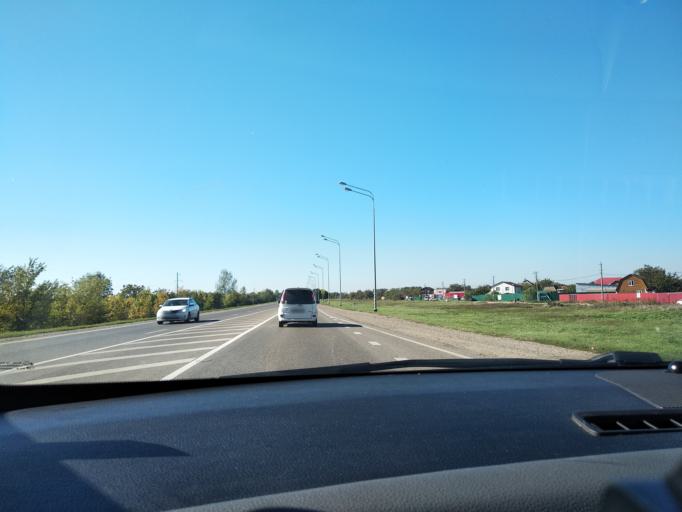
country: RU
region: Krasnodarskiy
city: Novotitarovskaya
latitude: 45.1576
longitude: 39.0735
